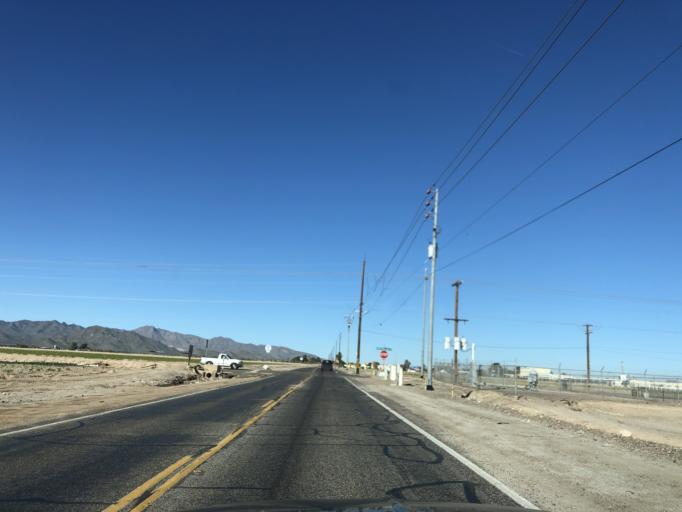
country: US
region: Arizona
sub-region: Maricopa County
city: Buckeye
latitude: 33.4204
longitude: -112.5042
